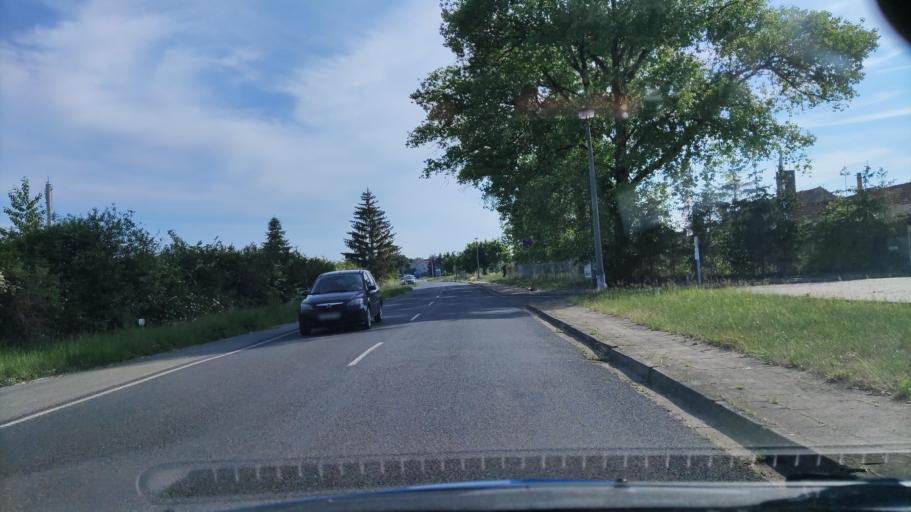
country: DE
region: Saxony-Anhalt
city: Klotze
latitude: 52.6357
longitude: 11.1755
